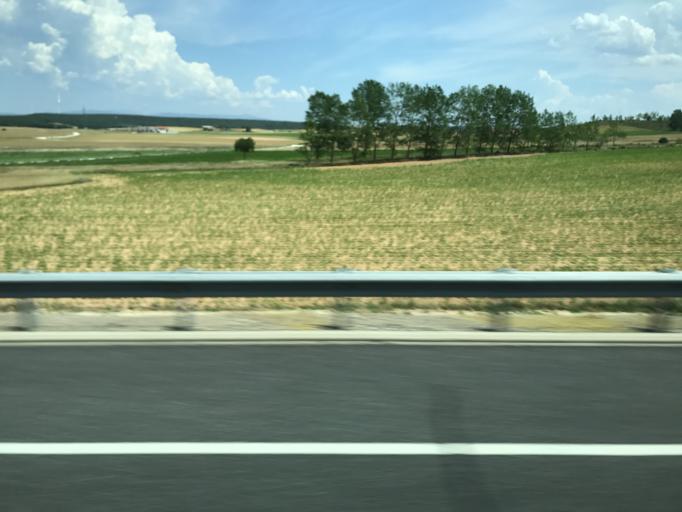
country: ES
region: Castille and Leon
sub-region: Provincia de Burgos
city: Cogollos
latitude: 42.1940
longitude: -3.6973
